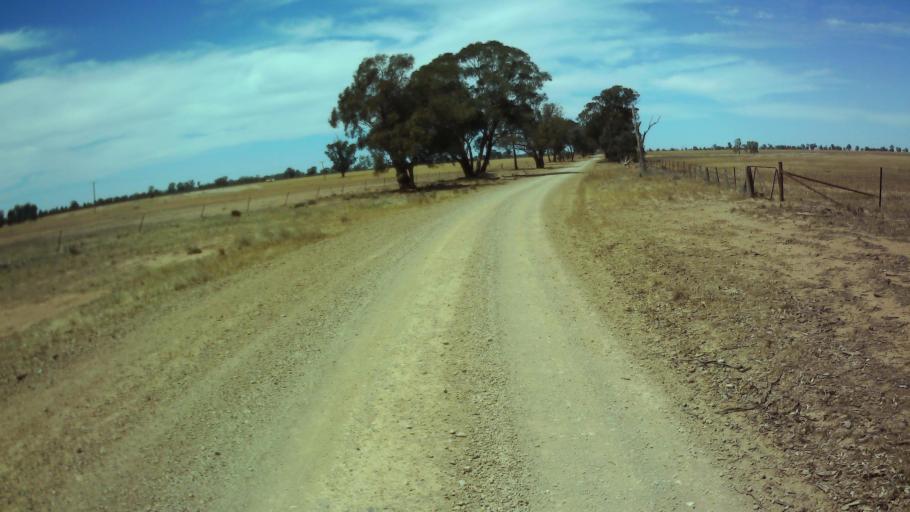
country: AU
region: New South Wales
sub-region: Weddin
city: Grenfell
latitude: -33.8651
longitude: 147.8072
